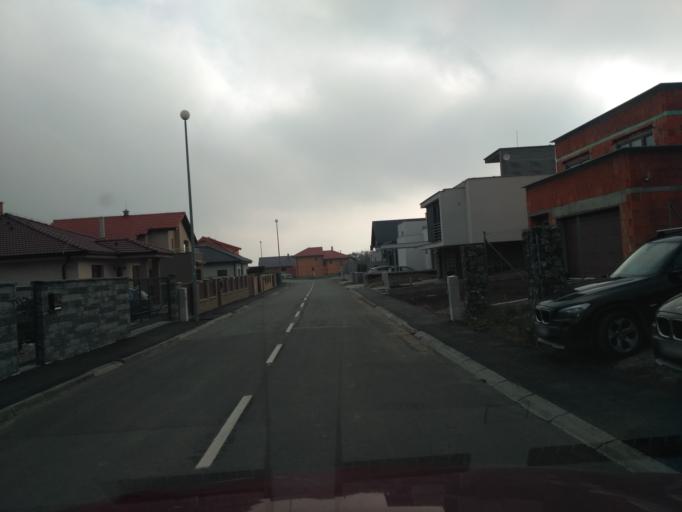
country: SK
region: Kosicky
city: Kosice
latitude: 48.6802
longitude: 21.3086
